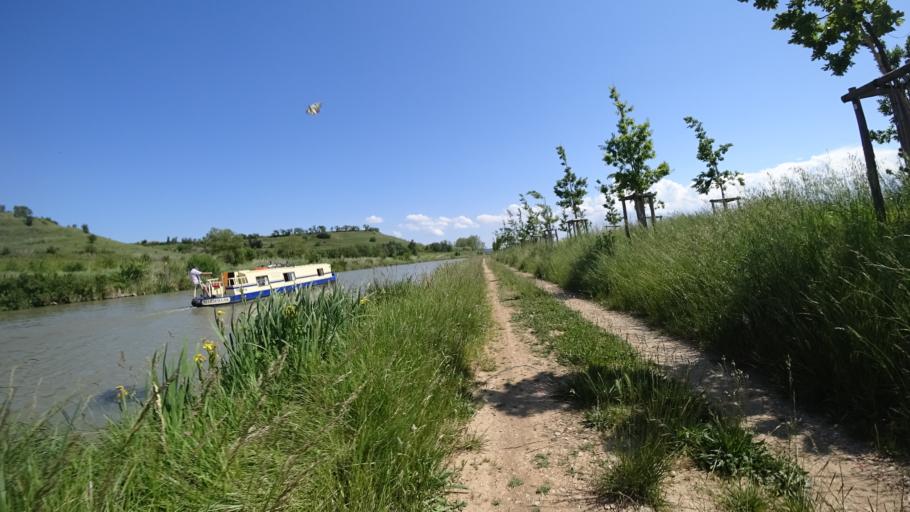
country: FR
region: Languedoc-Roussillon
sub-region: Departement de l'Aude
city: Canet
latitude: 43.2523
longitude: 2.8420
